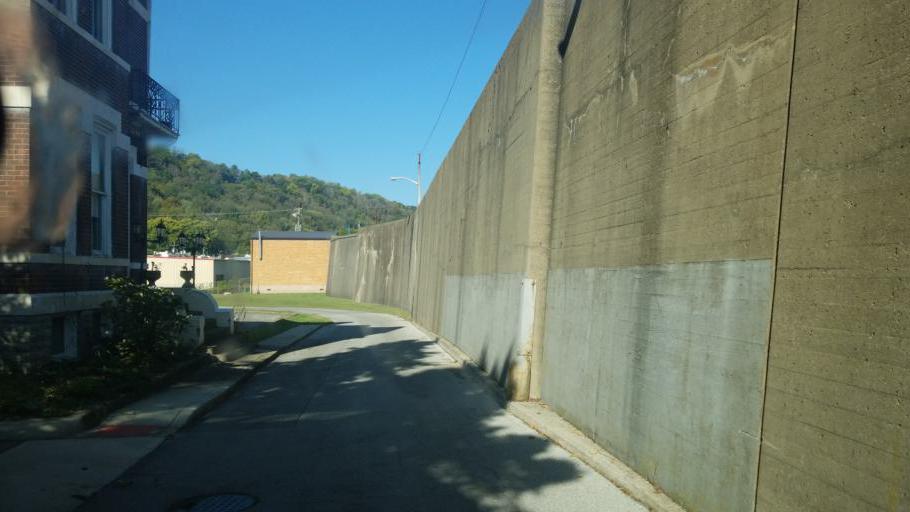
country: US
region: Ohio
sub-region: Brown County
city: Aberdeen
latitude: 38.6498
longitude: -83.7666
